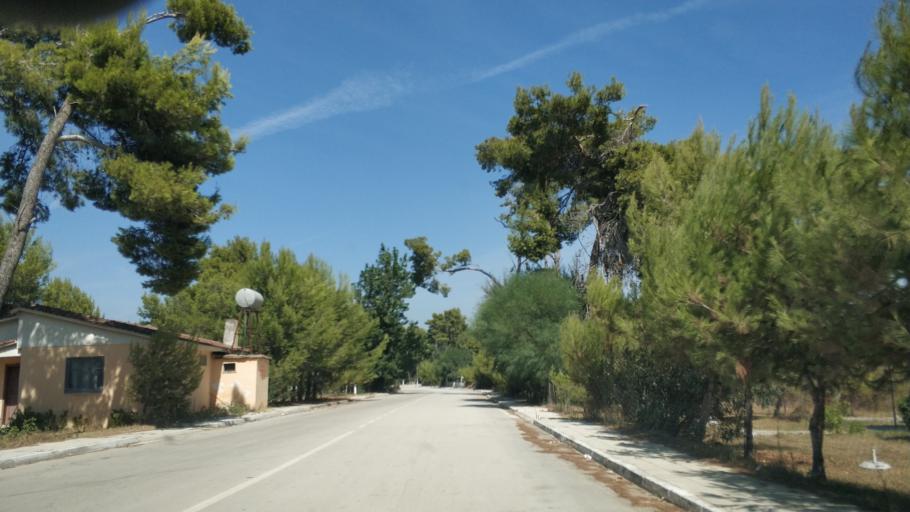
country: AL
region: Fier
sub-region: Rrethi i Lushnjes
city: Divjake
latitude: 40.9666
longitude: 19.4783
